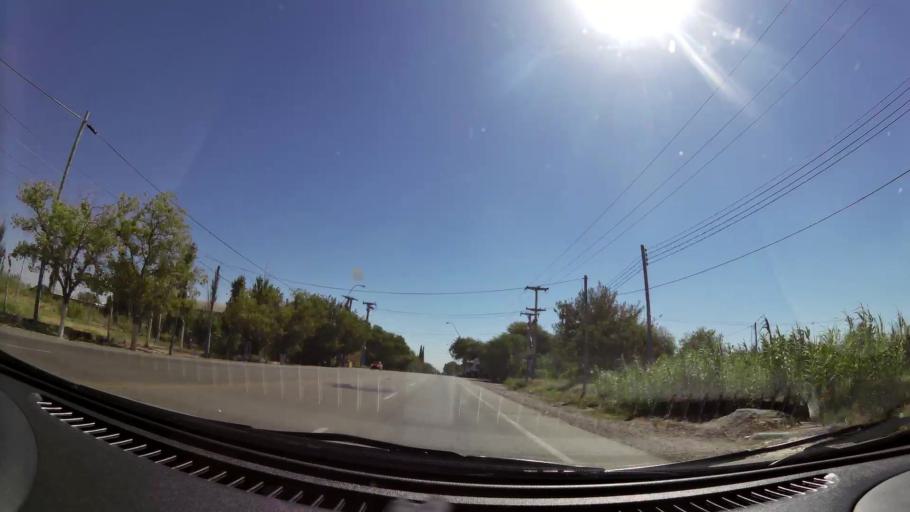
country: AR
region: San Juan
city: Villa Krause
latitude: -31.6021
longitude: -68.5425
